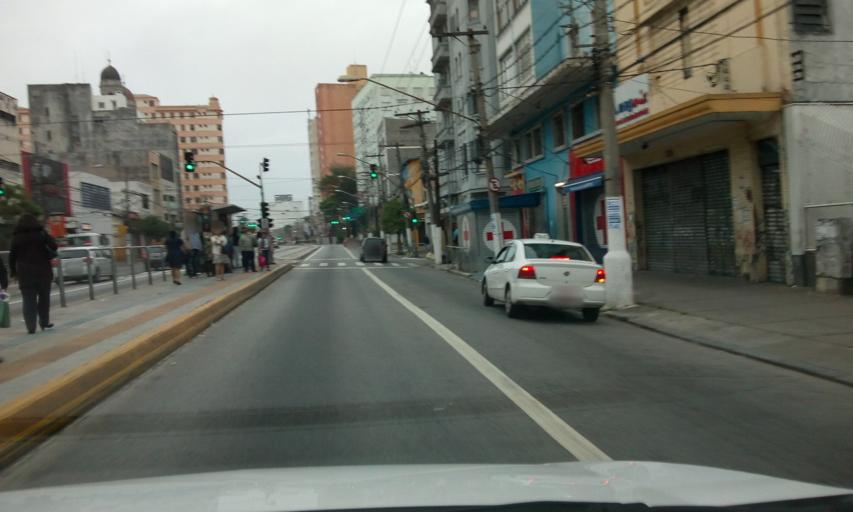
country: BR
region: Sao Paulo
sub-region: Sao Paulo
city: Sao Paulo
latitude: -23.5461
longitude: -46.6221
